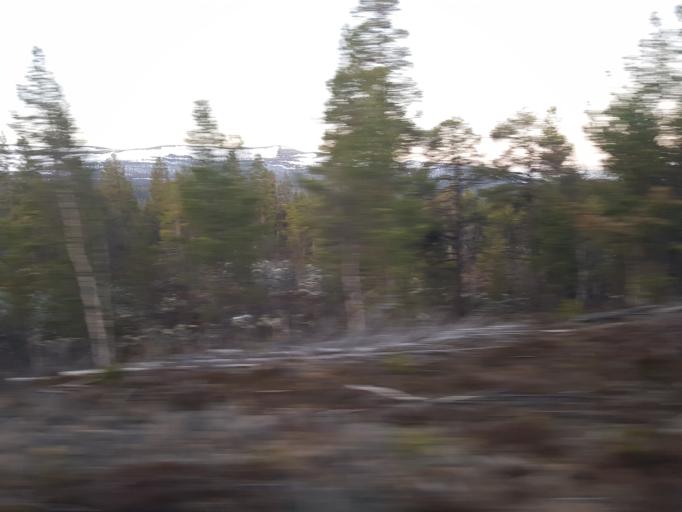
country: NO
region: Oppland
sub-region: Dovre
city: Dombas
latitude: 62.0992
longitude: 9.1753
